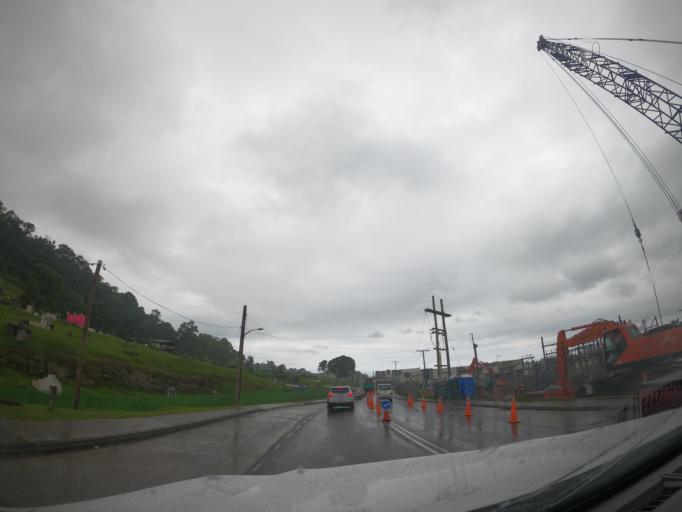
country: FJ
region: Central
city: Suva
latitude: -18.1156
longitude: 178.4313
